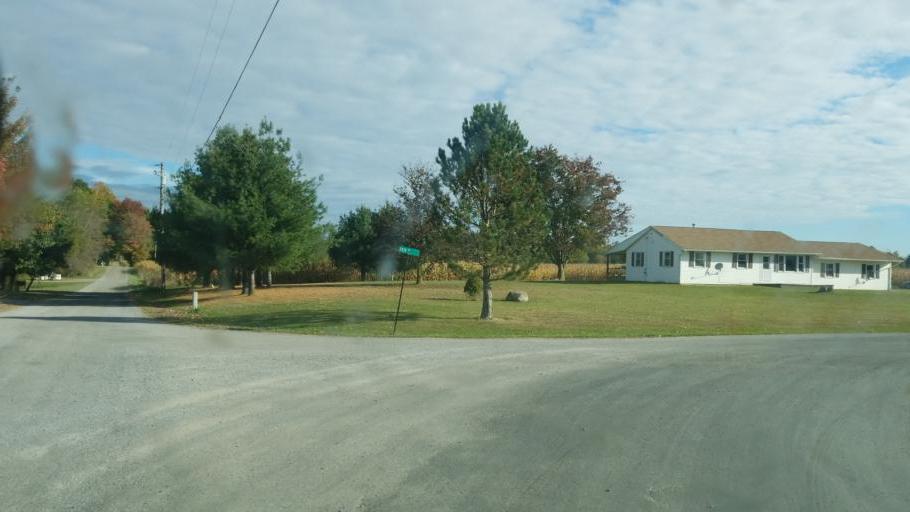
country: US
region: Pennsylvania
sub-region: Mercer County
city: Greenville
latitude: 41.3685
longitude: -80.2582
